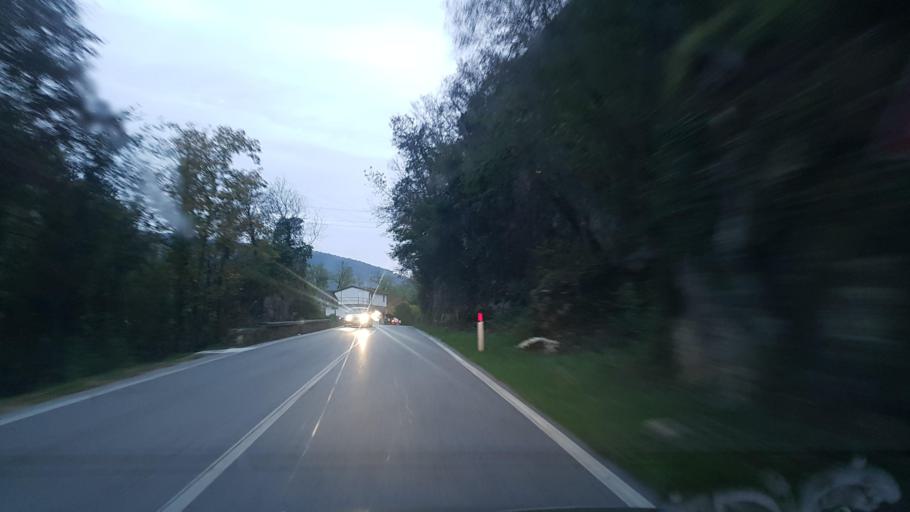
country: IT
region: Friuli Venezia Giulia
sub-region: Provincia di Pordenone
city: Anduins
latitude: 46.2129
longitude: 12.9553
